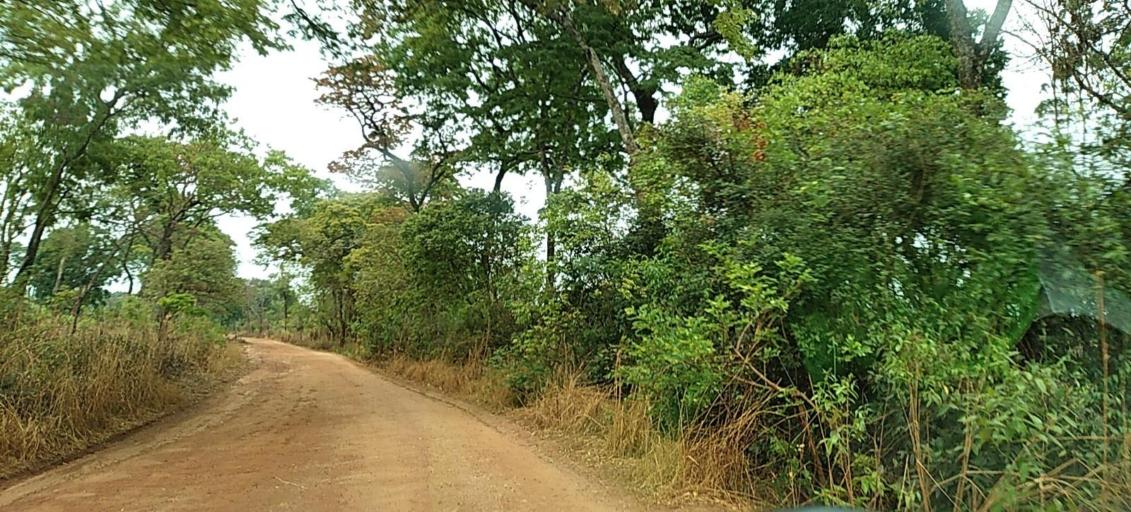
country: ZM
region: North-Western
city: Solwezi
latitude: -12.3251
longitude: 26.5204
